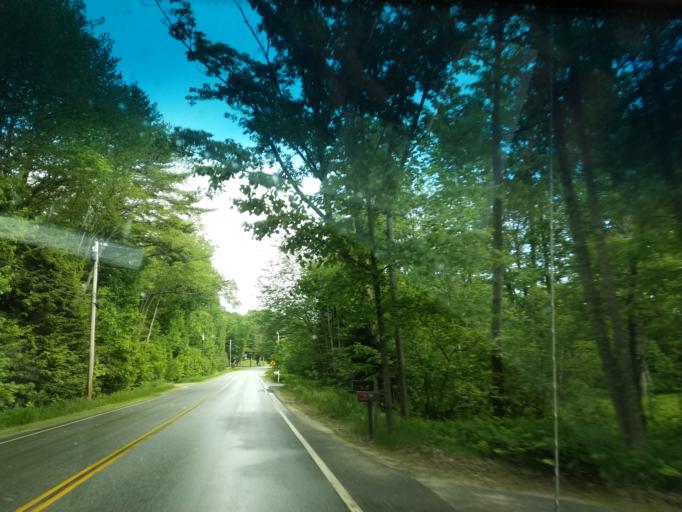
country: US
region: Maine
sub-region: Cumberland County
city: North Windham
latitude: 43.8022
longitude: -70.3688
